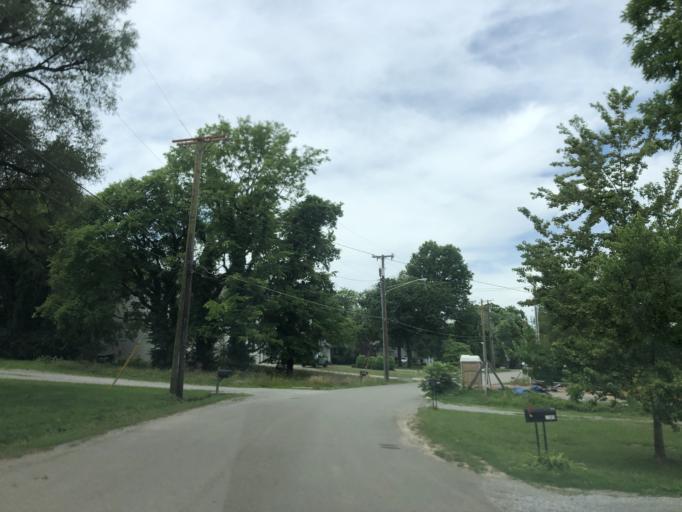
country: US
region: Tennessee
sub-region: Davidson County
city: Oak Hill
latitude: 36.1141
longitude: -86.7947
